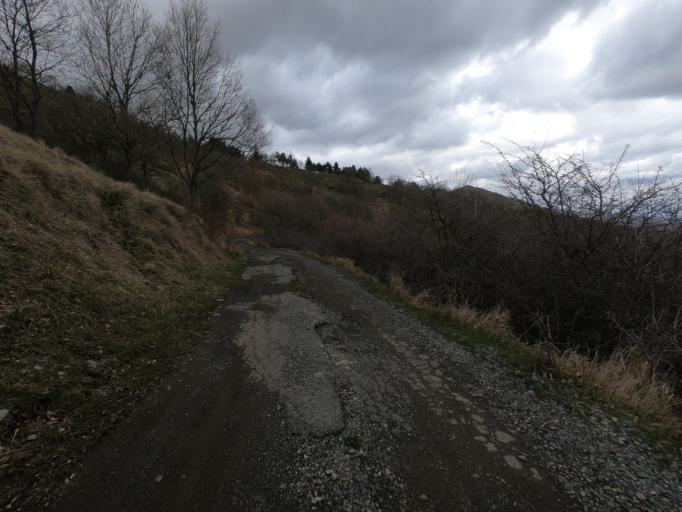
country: IT
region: Liguria
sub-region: Provincia di Imperia
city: Badalucco
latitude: 43.9128
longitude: 7.8789
